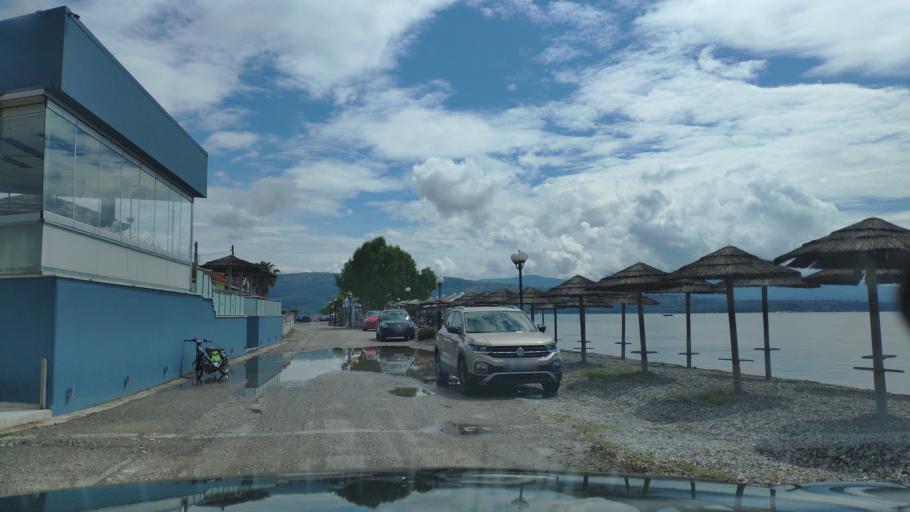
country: GR
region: West Greece
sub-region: Nomos Aitolias kai Akarnanias
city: Krikellos
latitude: 38.9293
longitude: 21.1409
